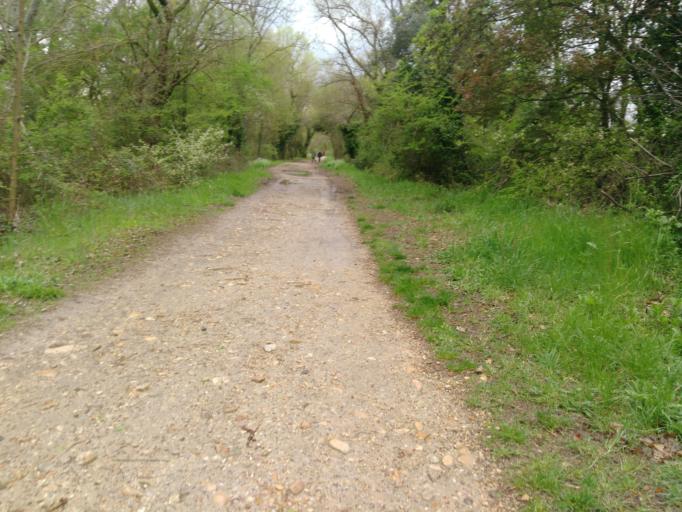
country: FR
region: Rhone-Alpes
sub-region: Departement de la Drome
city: Montboucher-sur-Jabron
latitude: 44.5453
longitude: 4.7779
